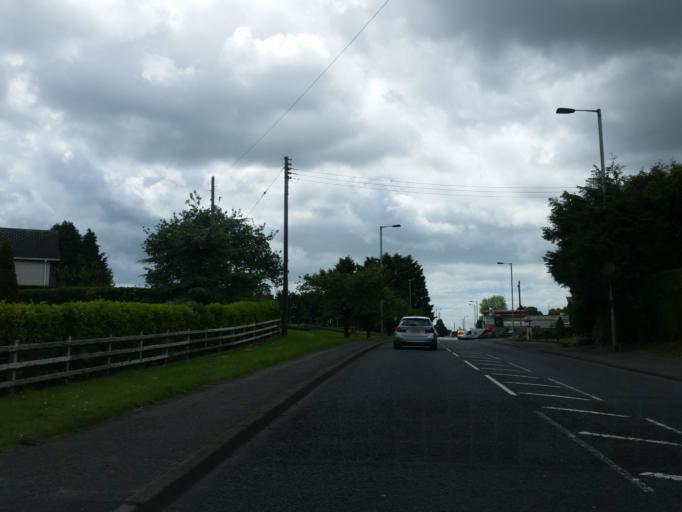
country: GB
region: Northern Ireland
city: Fivemiletown
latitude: 54.4152
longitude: -7.1626
